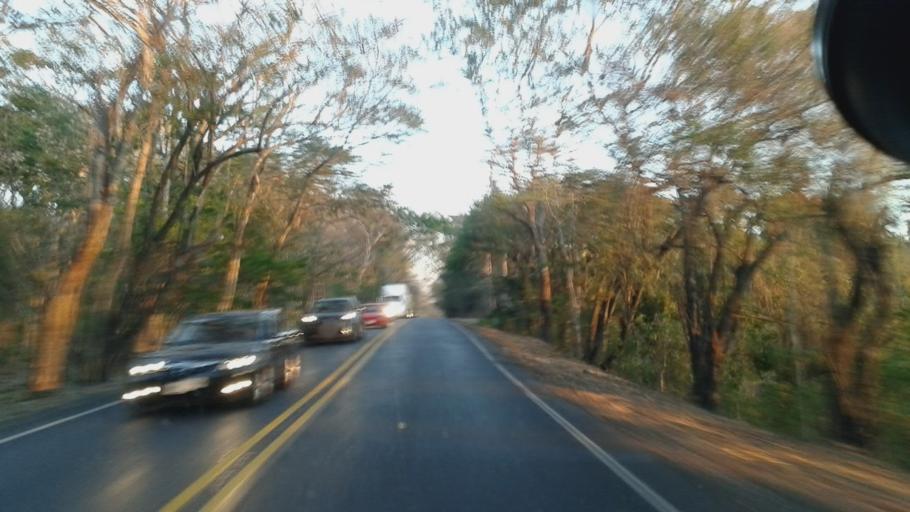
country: CR
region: Puntarenas
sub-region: Canton Central de Puntarenas
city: Puntarenas
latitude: 10.1274
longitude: -84.9010
